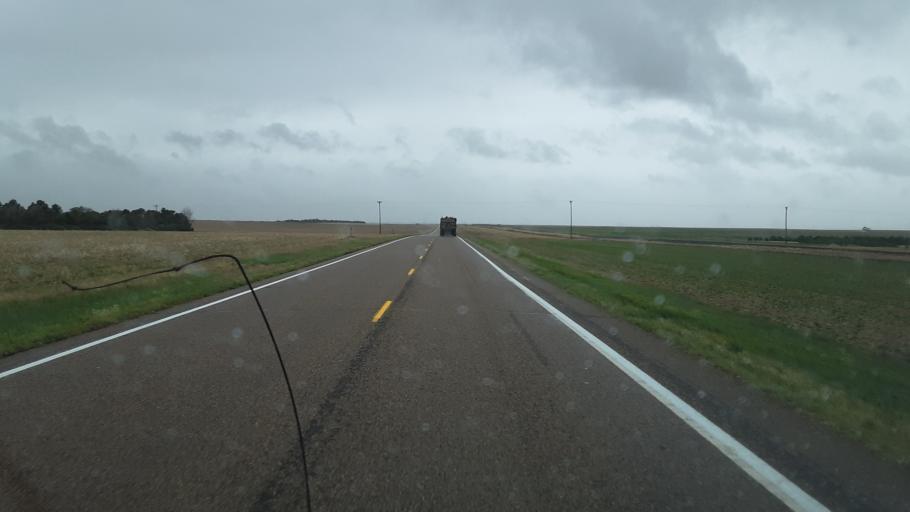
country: US
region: Colorado
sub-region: Cheyenne County
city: Cheyenne Wells
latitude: 38.8440
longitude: -102.2559
